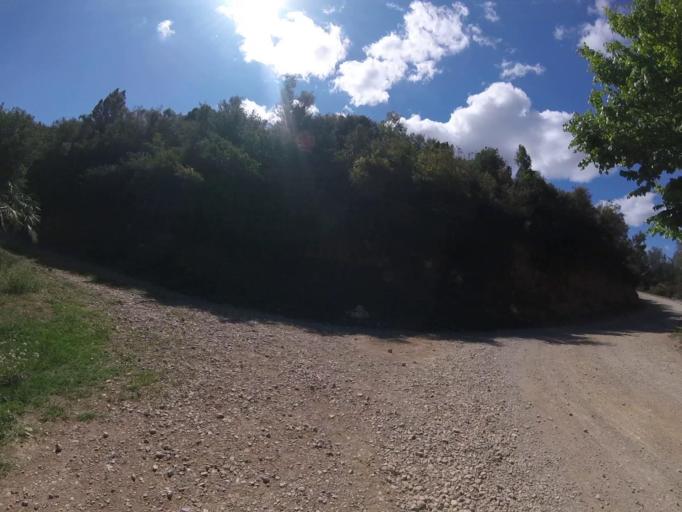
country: ES
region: Valencia
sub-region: Provincia de Castello
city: Santa Magdalena de Pulpis
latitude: 40.3259
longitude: 0.3372
